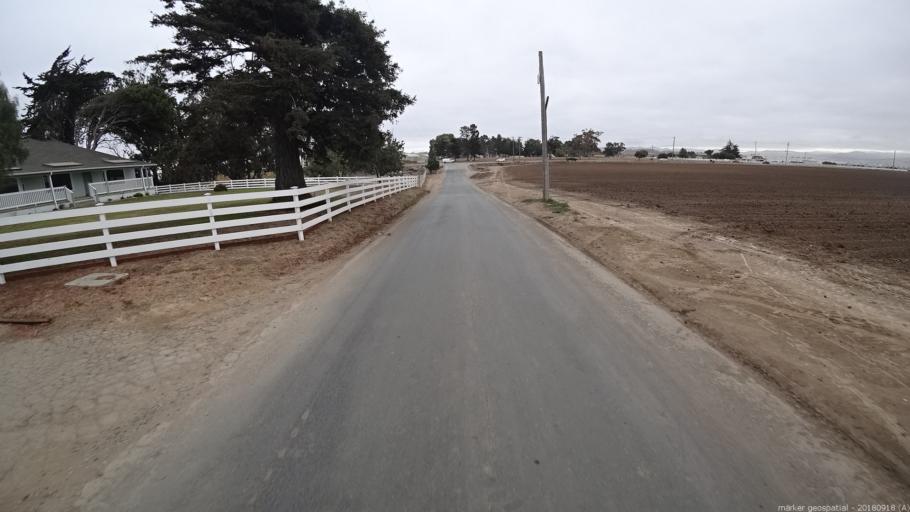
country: US
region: California
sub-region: Monterey County
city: Prunedale
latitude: 36.7429
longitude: -121.6920
